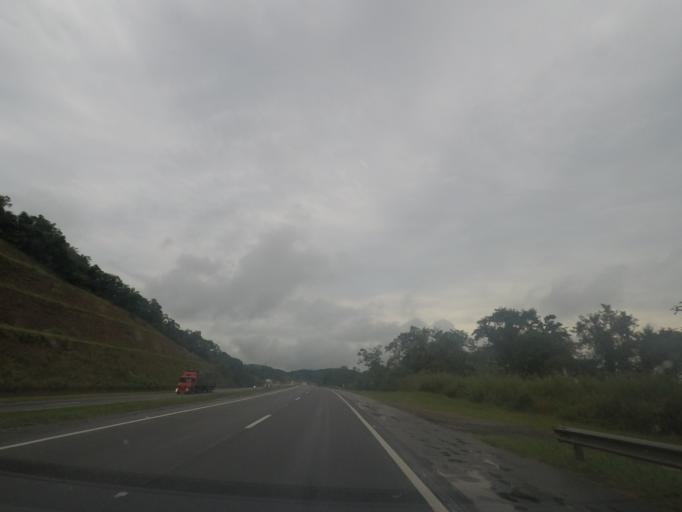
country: BR
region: Sao Paulo
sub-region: Jacupiranga
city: Jacupiranga
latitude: -24.6706
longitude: -47.9785
